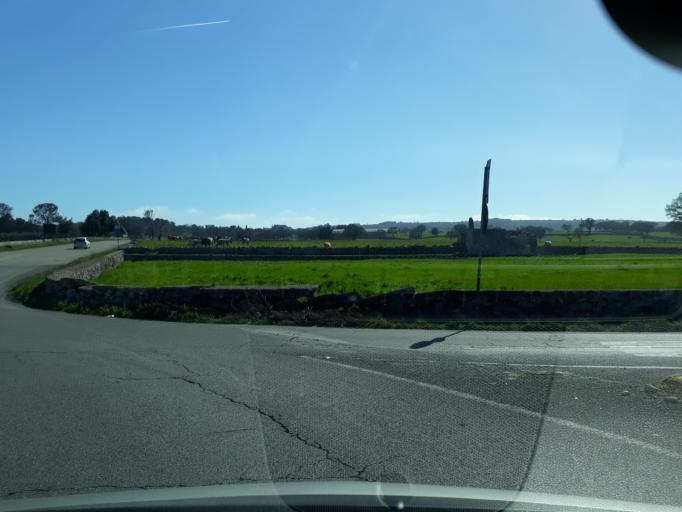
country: IT
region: Apulia
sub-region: Provincia di Bari
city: Alberobello
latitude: 40.8252
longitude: 17.2489
